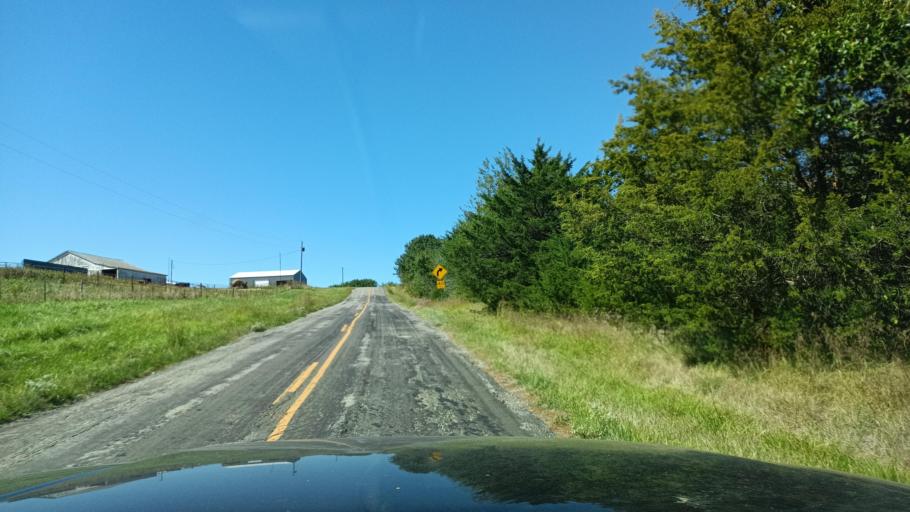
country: US
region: Missouri
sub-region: Scotland County
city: Memphis
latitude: 40.3483
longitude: -92.3282
